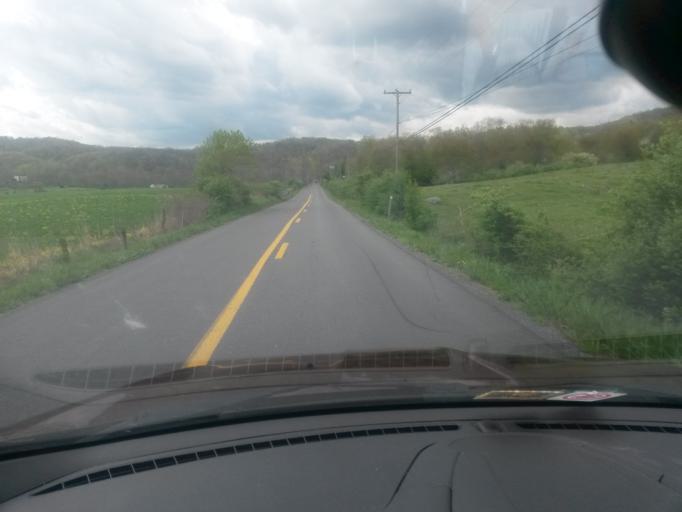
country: US
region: West Virginia
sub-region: Greenbrier County
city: Lewisburg
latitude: 37.9336
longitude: -80.3985
